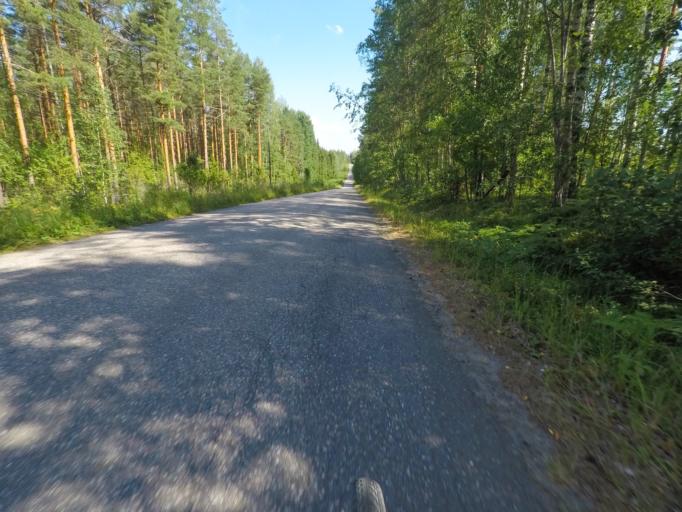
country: FI
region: Southern Savonia
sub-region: Mikkeli
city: Puumala
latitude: 61.4225
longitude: 28.1314
